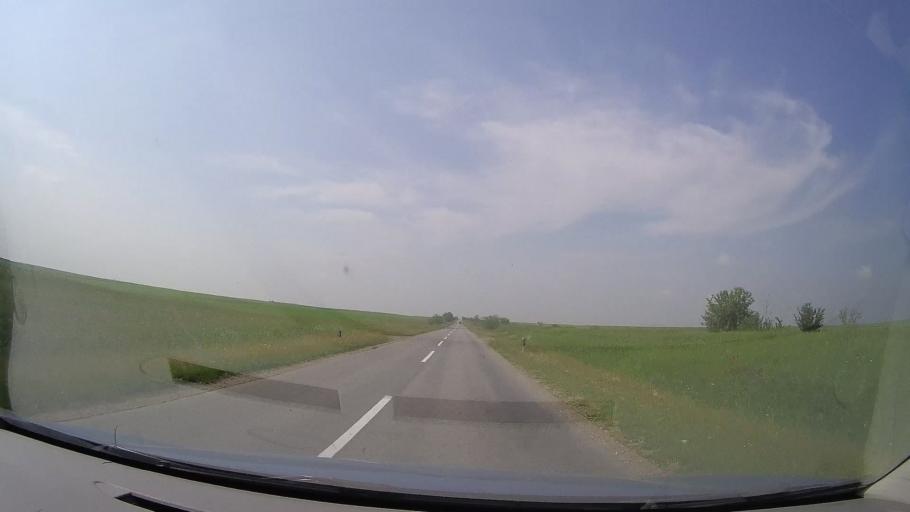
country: RS
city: Samos
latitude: 45.1731
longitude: 20.7567
